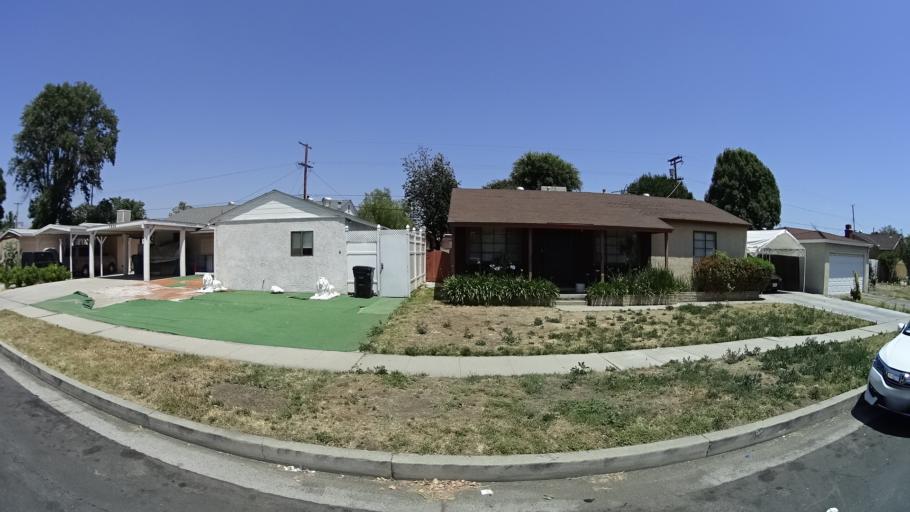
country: US
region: California
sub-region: Los Angeles County
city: Van Nuys
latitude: 34.2143
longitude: -118.4320
